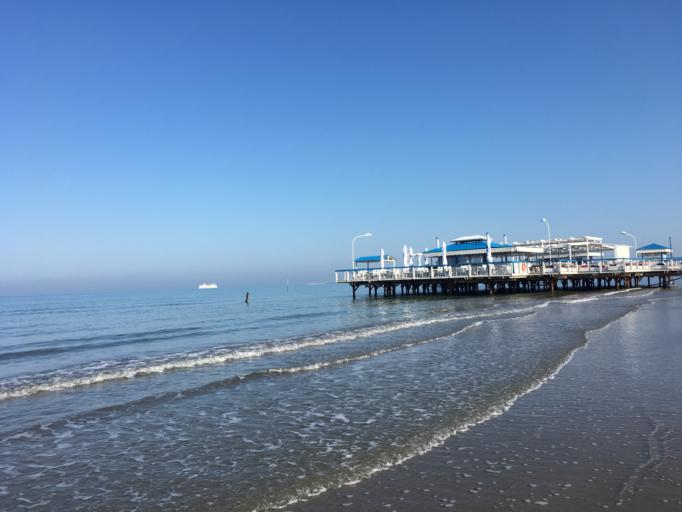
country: AL
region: Tirane
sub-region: Rrethi i Kavajes
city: Golem
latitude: 41.2798
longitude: 19.5124
